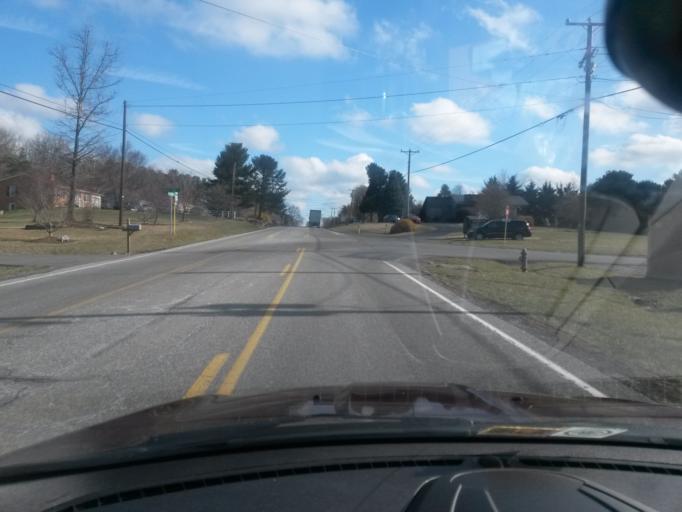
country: US
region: Virginia
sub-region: Augusta County
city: Jolivue
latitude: 38.0436
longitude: -79.1264
